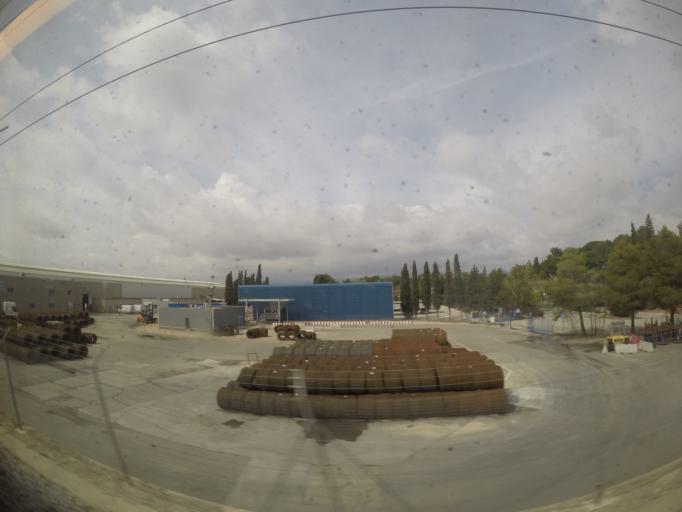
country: ES
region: Catalonia
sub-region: Provincia de Tarragona
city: Santa Oliva
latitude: 41.2627
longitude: 1.5872
